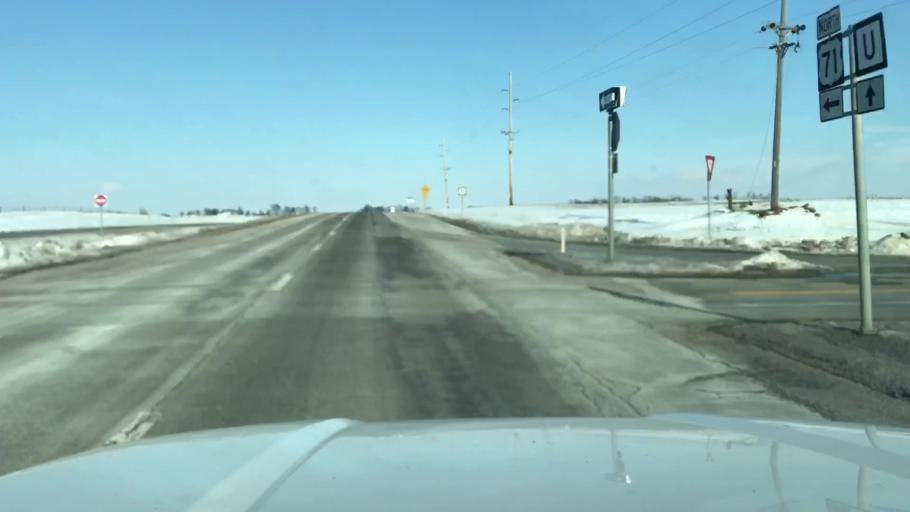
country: US
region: Missouri
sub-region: Nodaway County
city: Maryville
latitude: 40.2585
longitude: -94.8668
